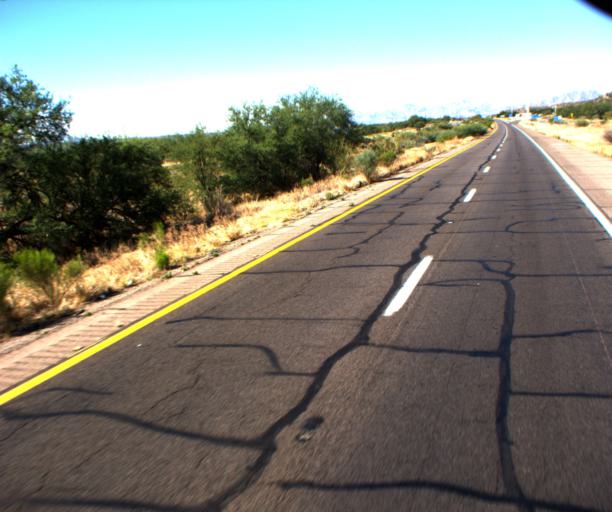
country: US
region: Arizona
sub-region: Pima County
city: Arivaca Junction
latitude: 31.7776
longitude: -111.0297
